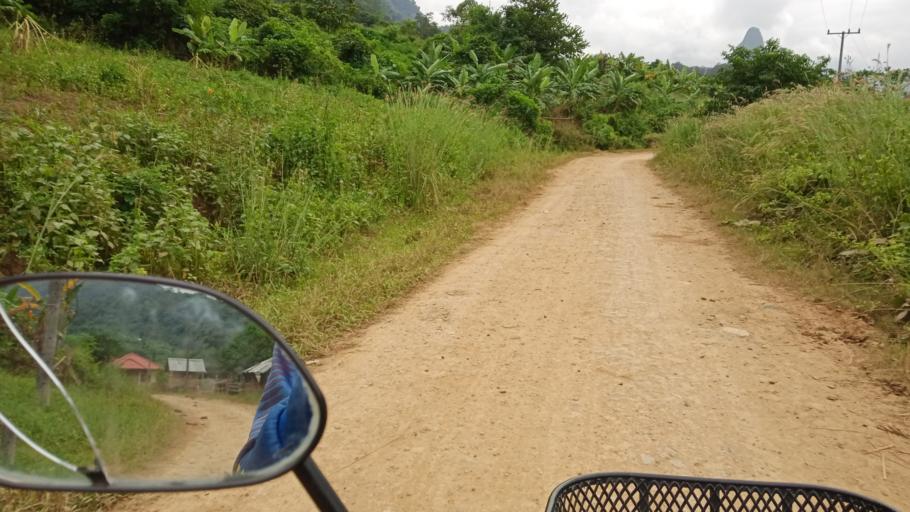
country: LA
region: Xiangkhoang
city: Phonsavan
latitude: 19.0920
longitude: 103.0048
